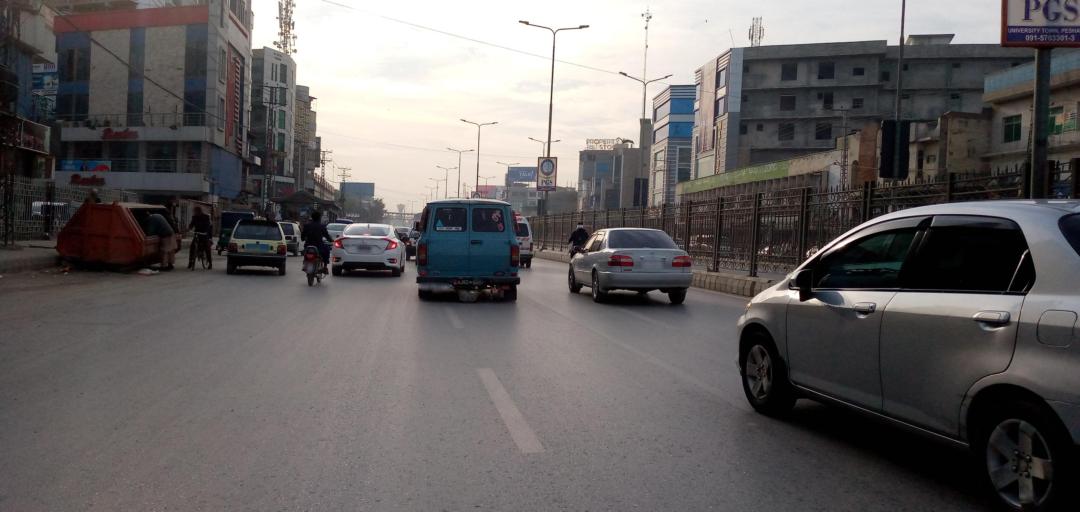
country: PK
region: Khyber Pakhtunkhwa
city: Peshawar
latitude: 34.0013
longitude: 71.4987
